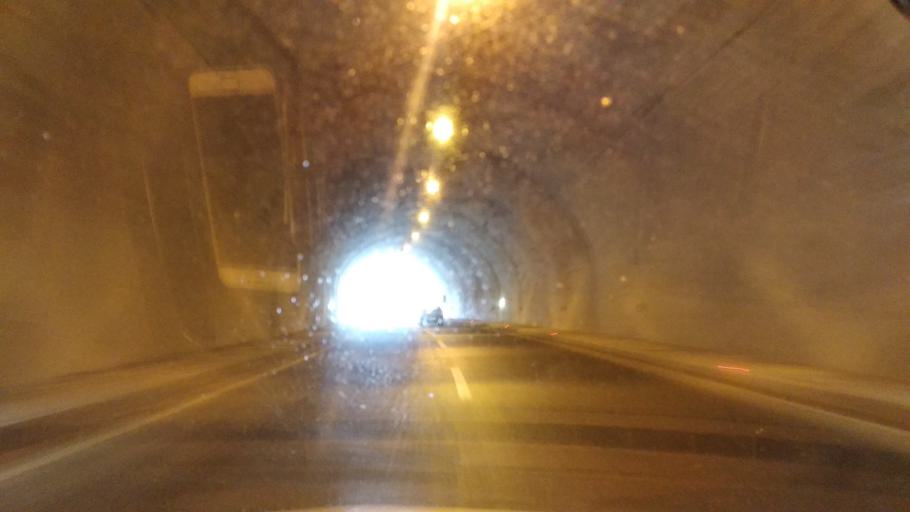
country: TR
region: Gumushane
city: Torul
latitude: 40.5474
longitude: 39.3219
